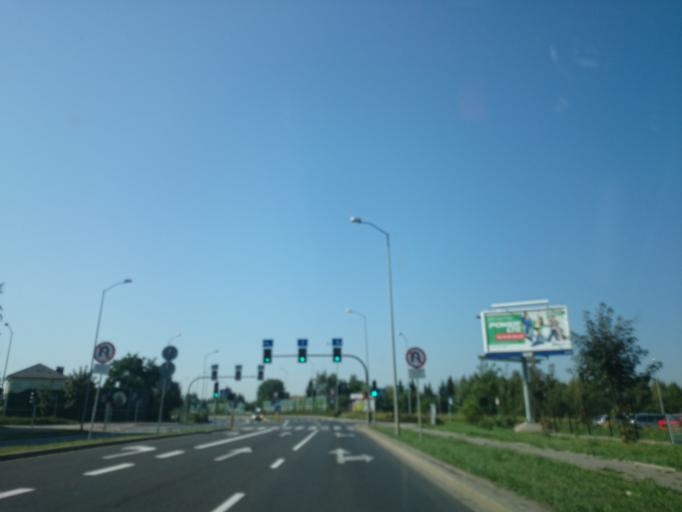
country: PL
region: West Pomeranian Voivodeship
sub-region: Powiat policki
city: Przeclaw
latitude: 53.4100
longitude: 14.4912
